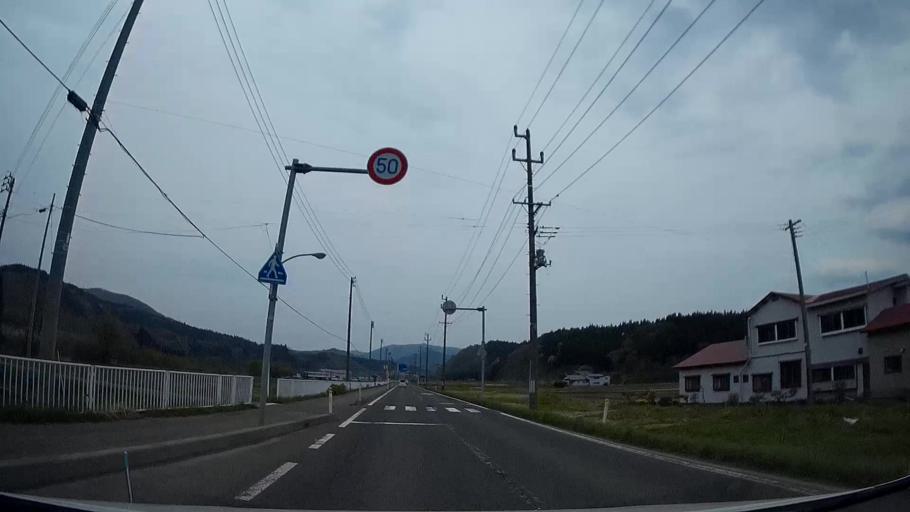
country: JP
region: Akita
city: Hanawa
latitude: 40.2860
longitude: 140.8056
